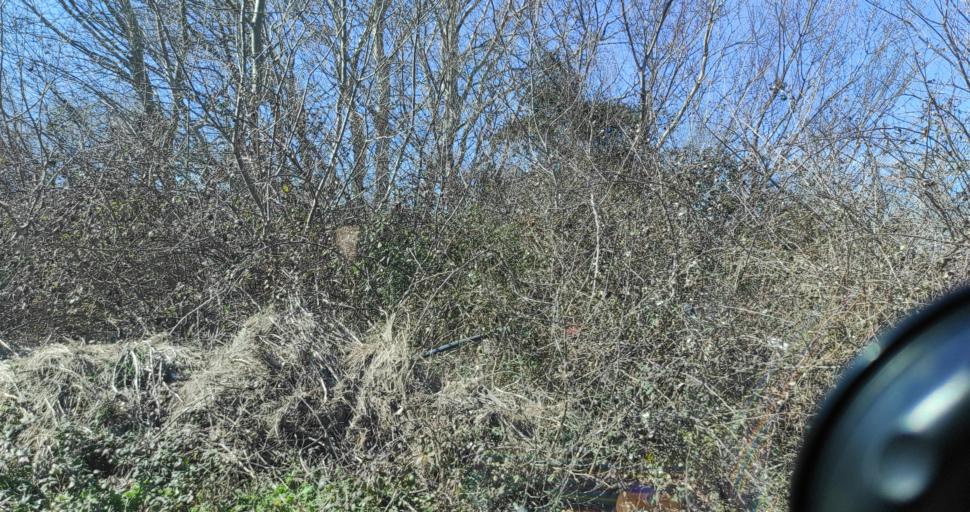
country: AL
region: Shkoder
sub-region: Rrethi i Shkodres
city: Velipoje
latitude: 41.8662
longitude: 19.4190
